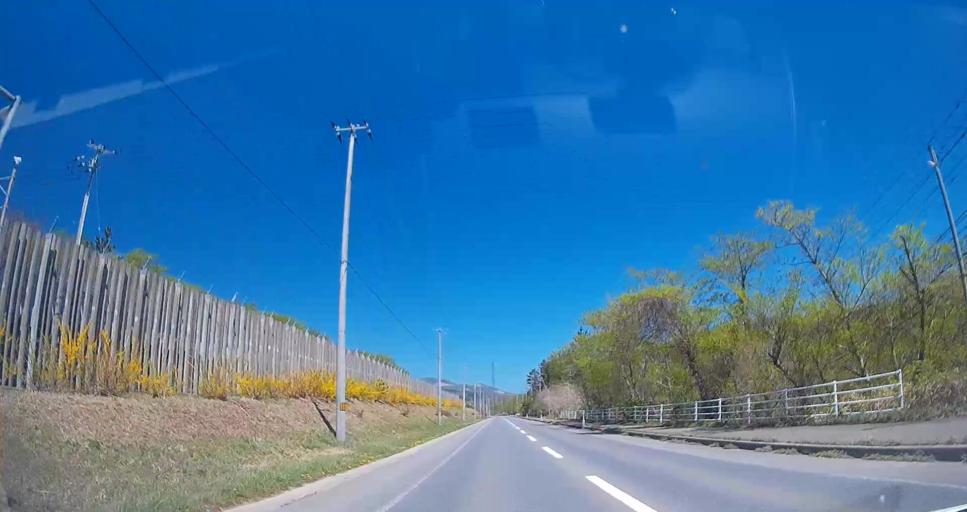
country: JP
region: Aomori
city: Misawa
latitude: 40.9758
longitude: 141.3595
